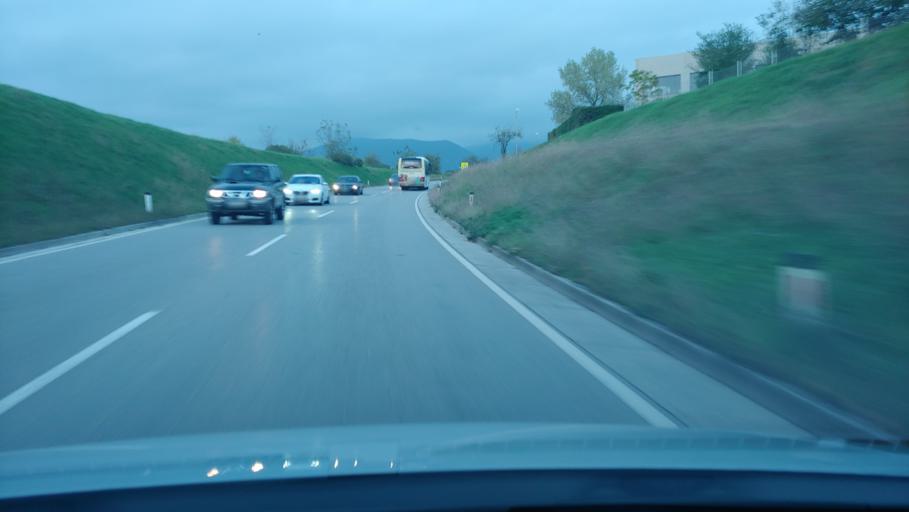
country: SI
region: Sempeter-Vrtojba
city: Sempeter pri Gorici
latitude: 45.9240
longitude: 13.6291
